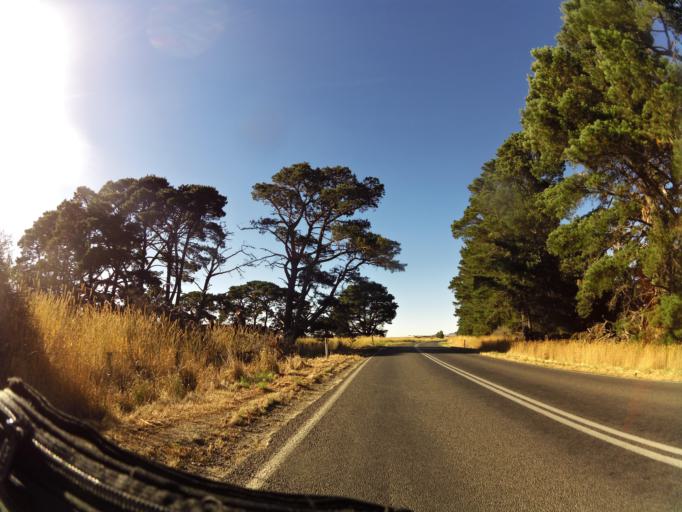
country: AU
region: Victoria
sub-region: Ballarat North
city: Delacombe
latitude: -37.5506
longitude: 143.3683
